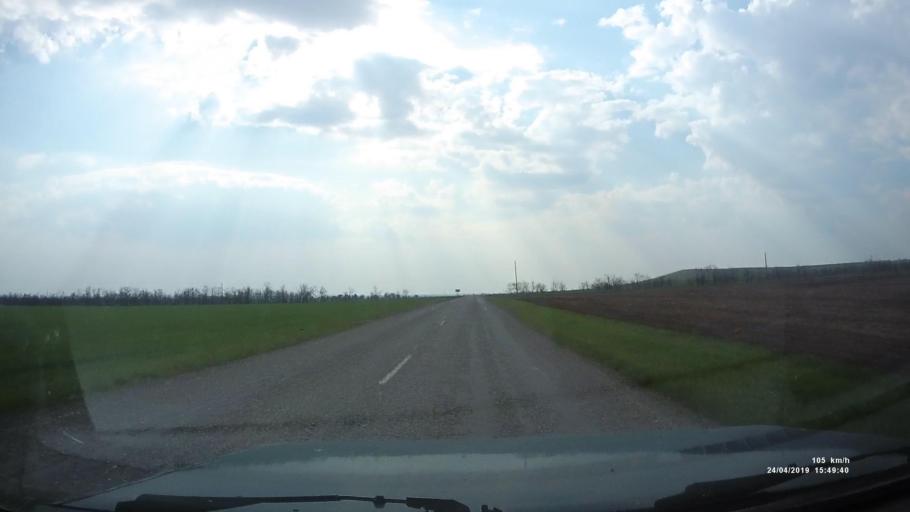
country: RU
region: Kalmykiya
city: Yashalta
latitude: 46.6042
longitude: 42.6502
